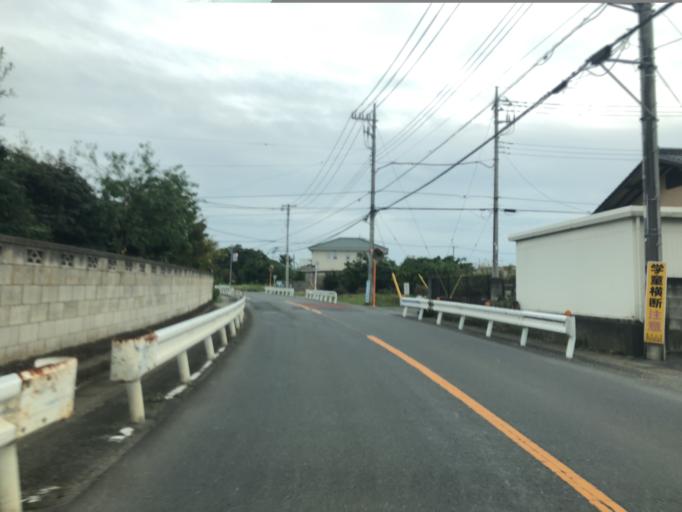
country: JP
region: Saitama
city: Fukiage-fujimi
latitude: 36.0498
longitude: 139.3901
